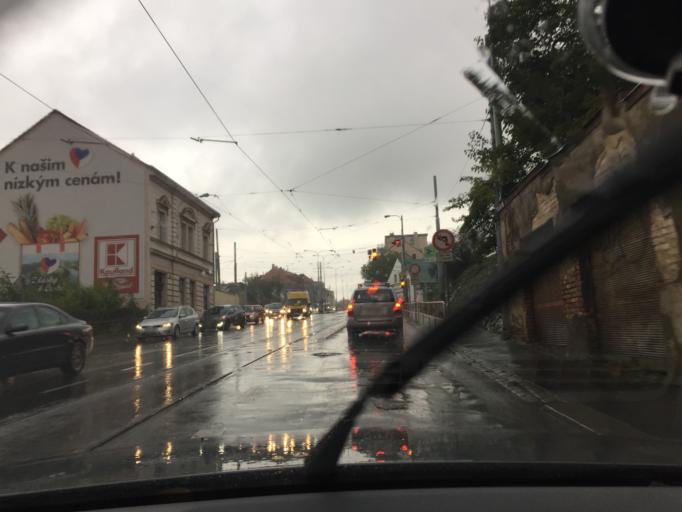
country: CZ
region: Praha
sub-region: Praha 8
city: Liben
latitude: 50.1212
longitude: 14.4562
